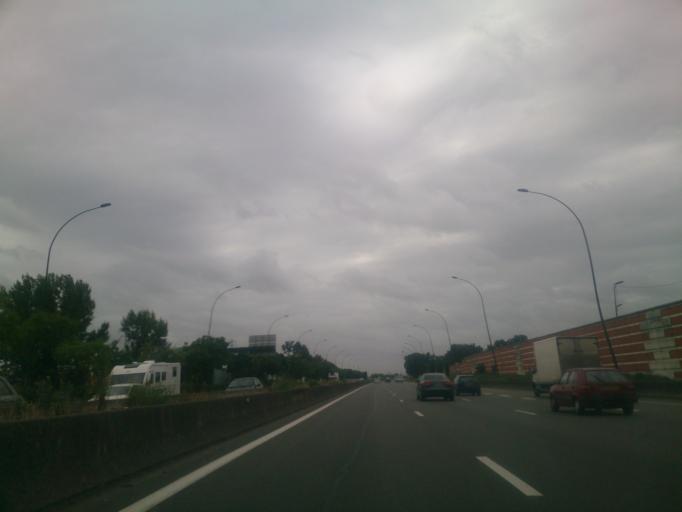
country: FR
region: Midi-Pyrenees
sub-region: Departement de la Haute-Garonne
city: Portet-sur-Garonne
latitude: 43.5523
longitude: 1.4079
